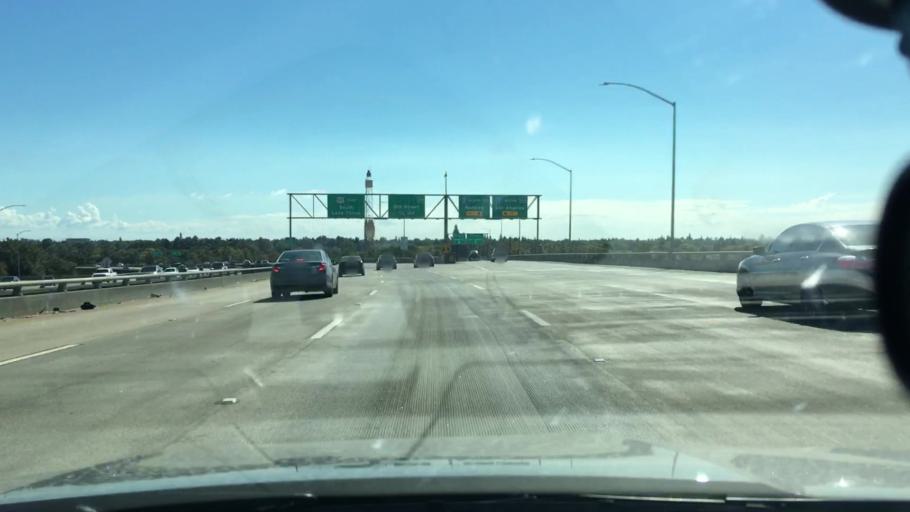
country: US
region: California
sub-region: Yolo County
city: West Sacramento
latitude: 38.5702
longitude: -121.5149
